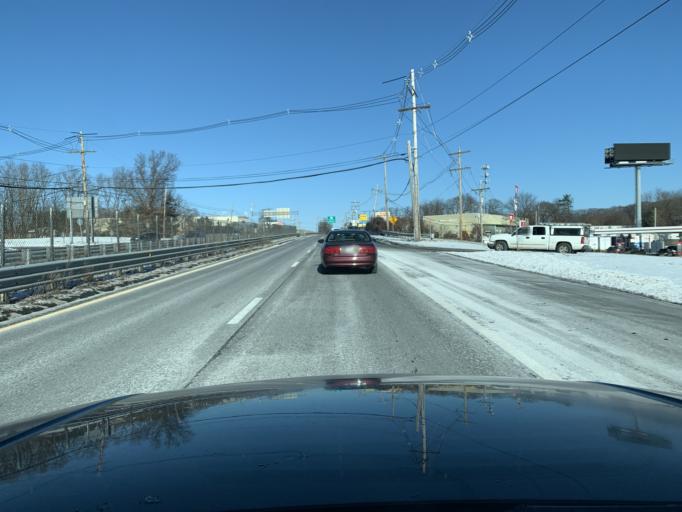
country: US
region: Massachusetts
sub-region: Essex County
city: South Peabody
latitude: 42.5473
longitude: -70.9836
